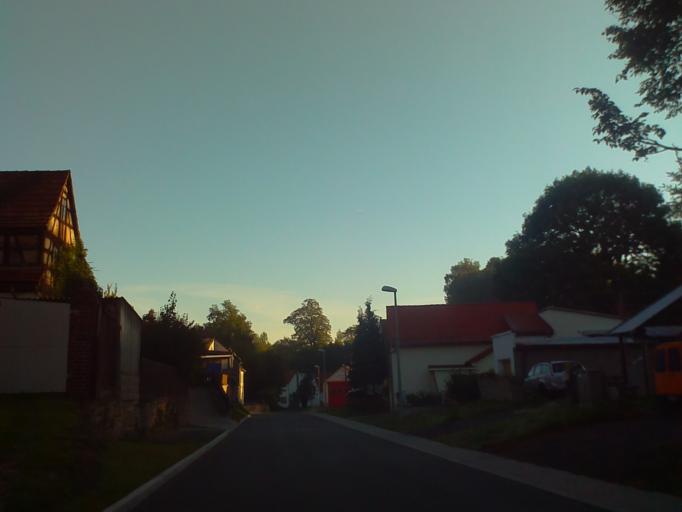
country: DE
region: Thuringia
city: Lindenkreuz
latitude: 50.8430
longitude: 11.9145
